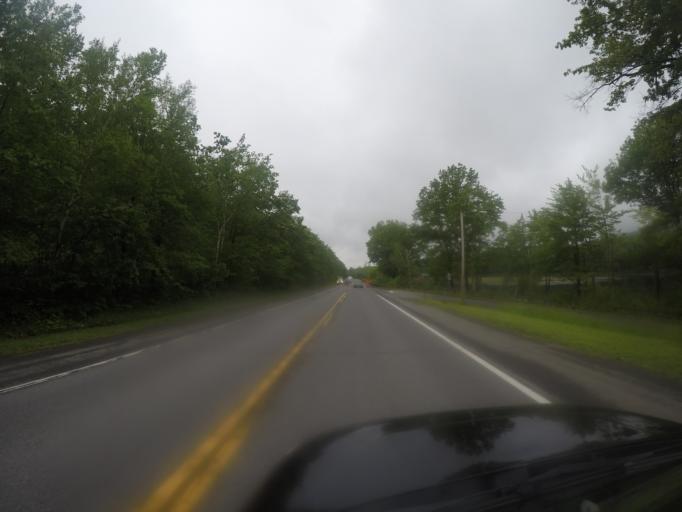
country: US
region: New York
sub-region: Ulster County
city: Shokan
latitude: 41.9905
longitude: -74.1683
